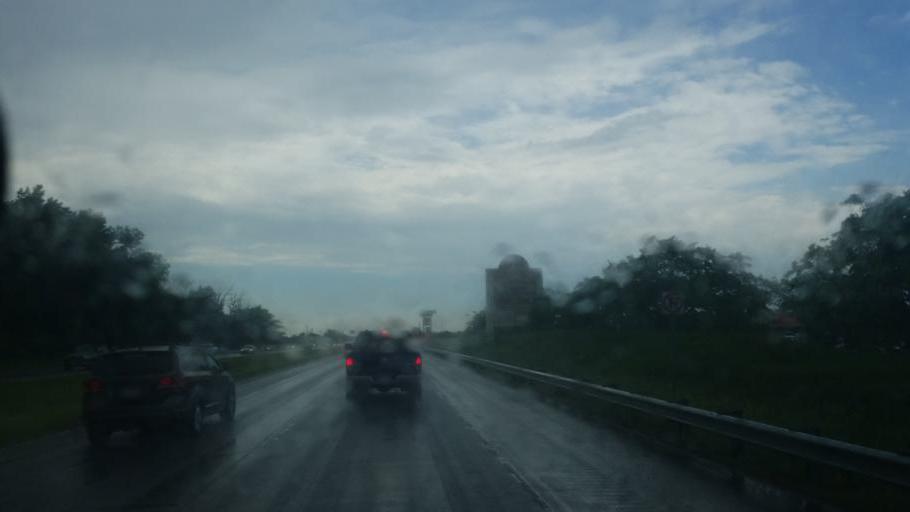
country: US
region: Indiana
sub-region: Whitley County
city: Columbia City
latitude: 41.1694
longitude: -85.4968
